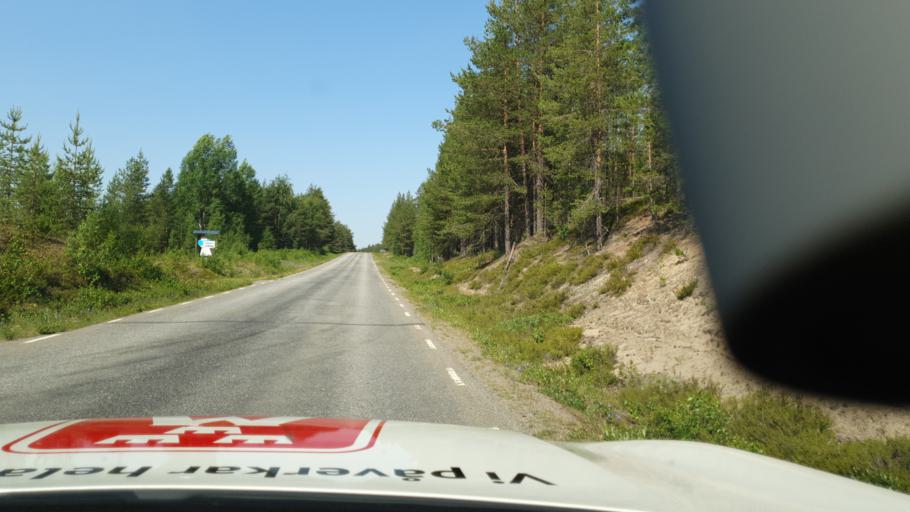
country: SE
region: Vaesterbotten
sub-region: Skelleftea Kommun
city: Langsele
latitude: 64.9578
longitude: 19.9074
